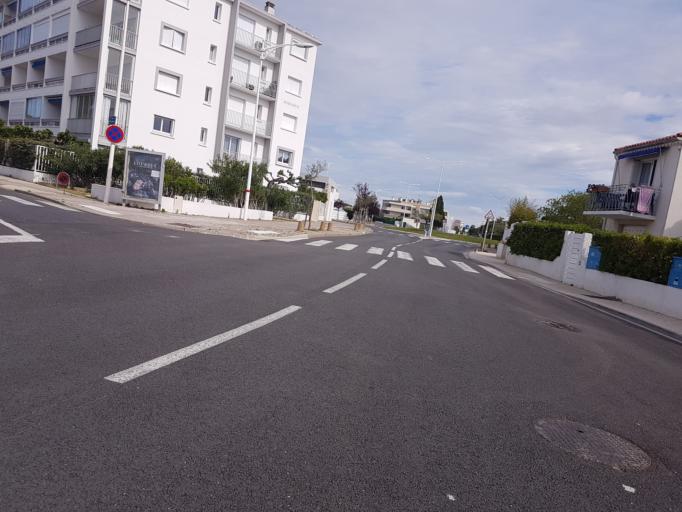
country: FR
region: Languedoc-Roussillon
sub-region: Departement du Gard
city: Le Grau-du-Roi
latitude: 43.5436
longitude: 4.1329
